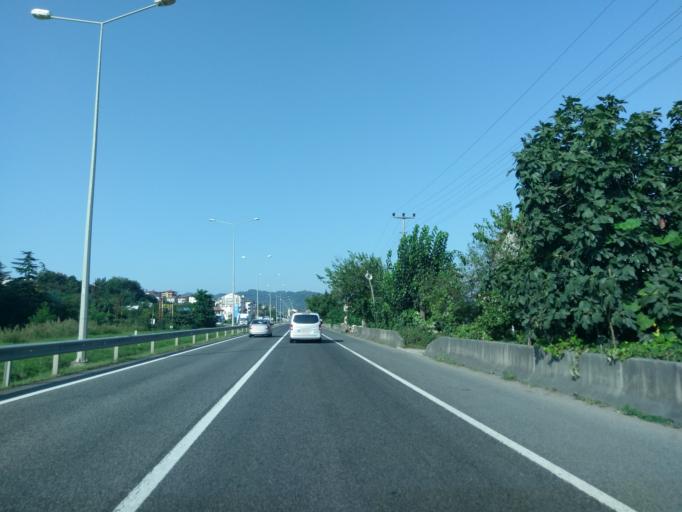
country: TR
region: Ordu
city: Bolaman
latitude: 41.0231
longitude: 37.5485
